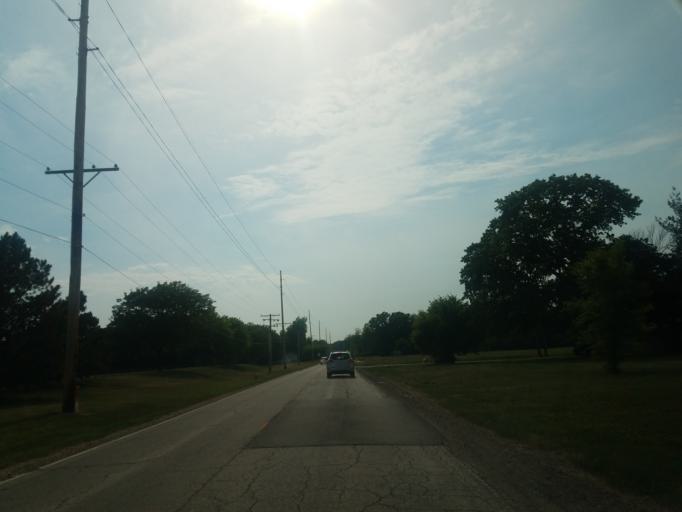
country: US
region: Illinois
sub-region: McLean County
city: Bloomington
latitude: 40.4514
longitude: -88.9740
